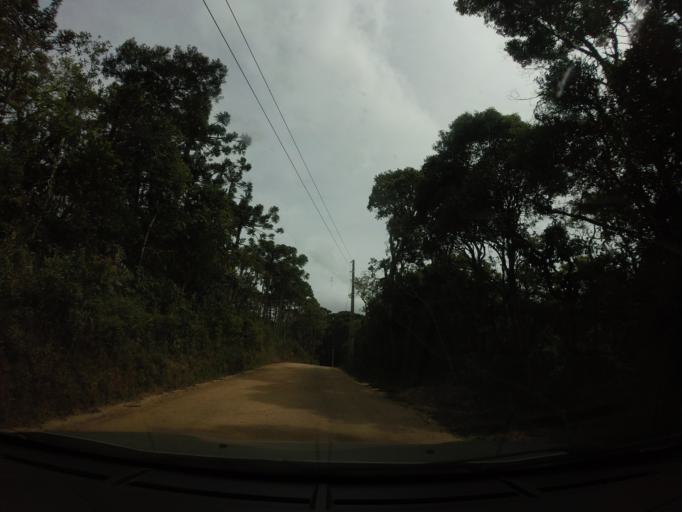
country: BR
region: Sao Paulo
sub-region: Campos Do Jordao
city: Campos do Jordao
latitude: -22.6777
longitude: -45.6457
